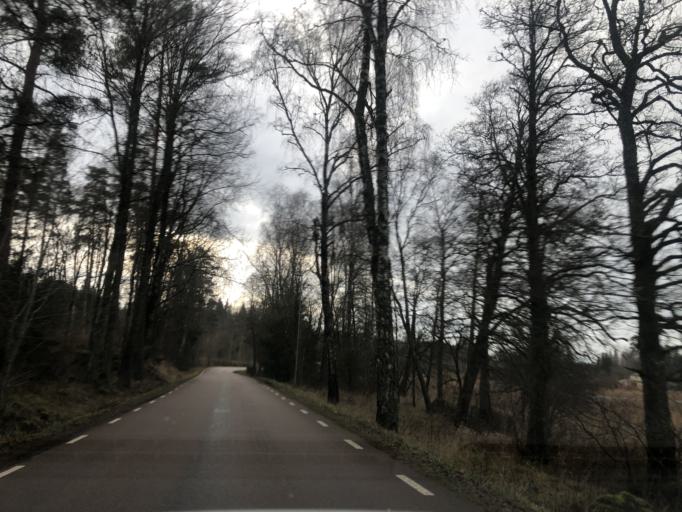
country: SE
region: Vaestra Goetaland
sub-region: Boras Kommun
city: Dalsjofors
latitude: 57.8178
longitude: 13.1478
